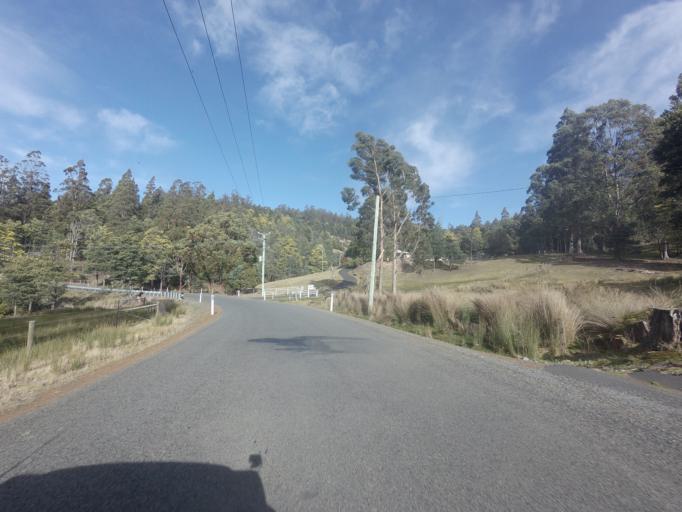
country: AU
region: Tasmania
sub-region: Kingborough
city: Margate
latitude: -43.0132
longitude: 147.1599
